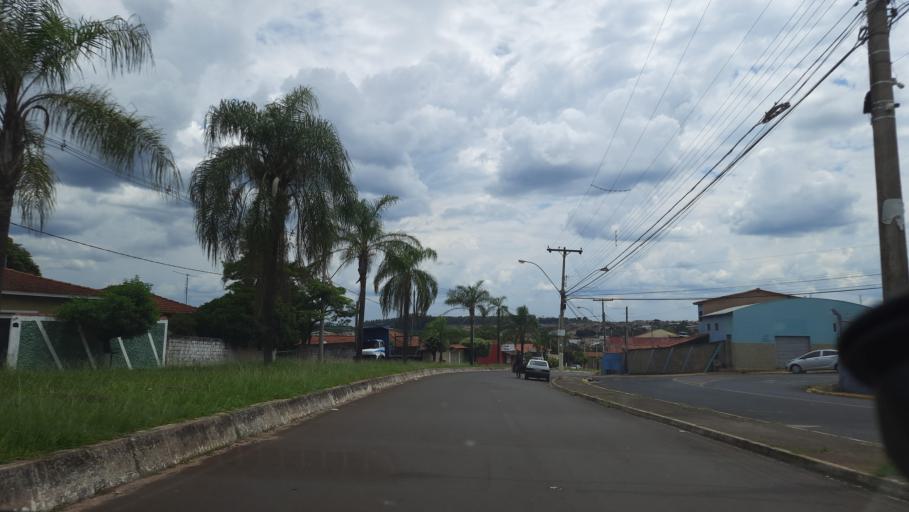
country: BR
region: Sao Paulo
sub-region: Cajuru
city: Cajuru
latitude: -21.2757
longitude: -47.2953
